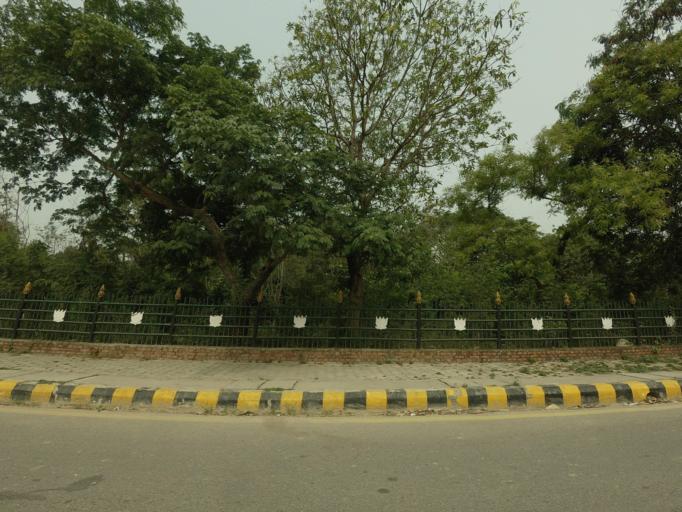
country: IN
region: Uttar Pradesh
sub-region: Maharajganj
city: Nautanwa
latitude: 27.4718
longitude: 83.2838
